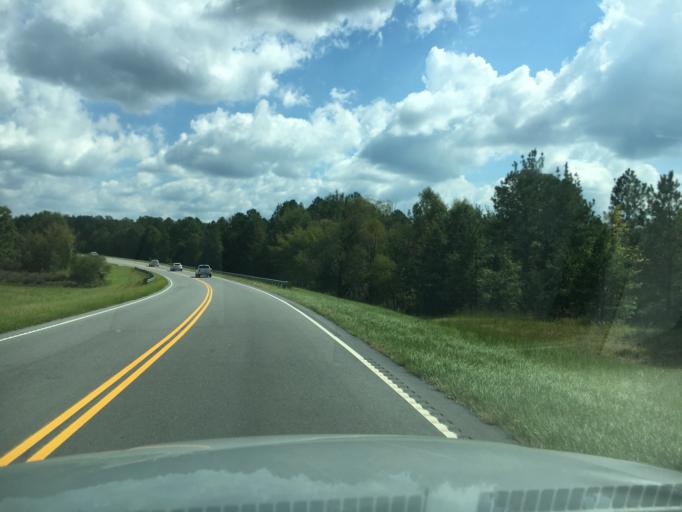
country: US
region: South Carolina
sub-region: Greenwood County
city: Greenwood
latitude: 34.1381
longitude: -82.1422
